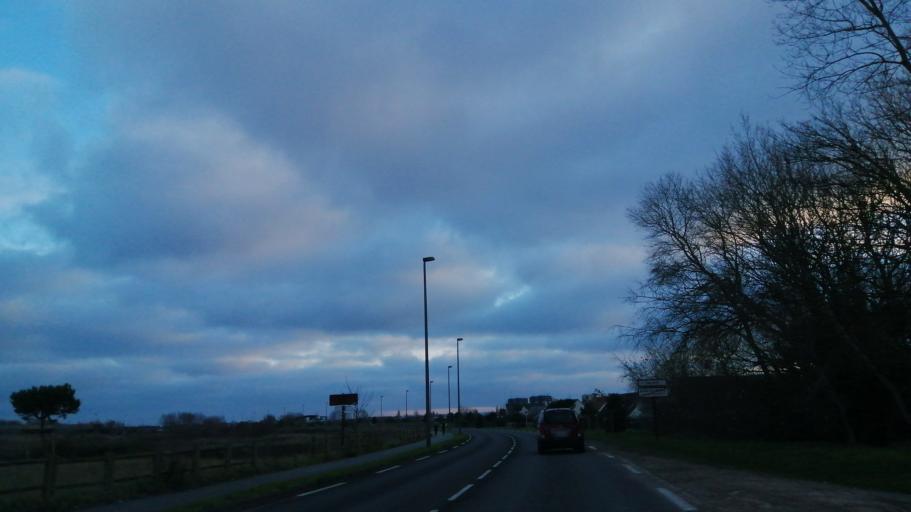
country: FR
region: Nord-Pas-de-Calais
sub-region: Departement du Pas-de-Calais
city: Calais
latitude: 50.9572
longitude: 1.8279
